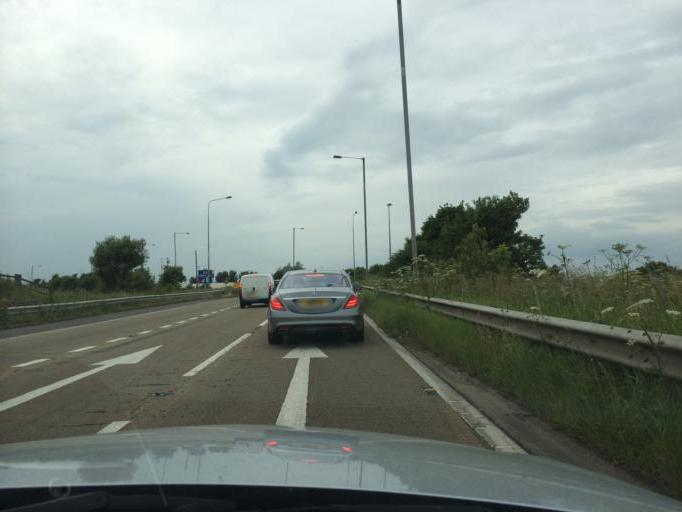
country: GB
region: England
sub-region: Borough of Bolton
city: Horwich
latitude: 53.5732
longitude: -2.5441
